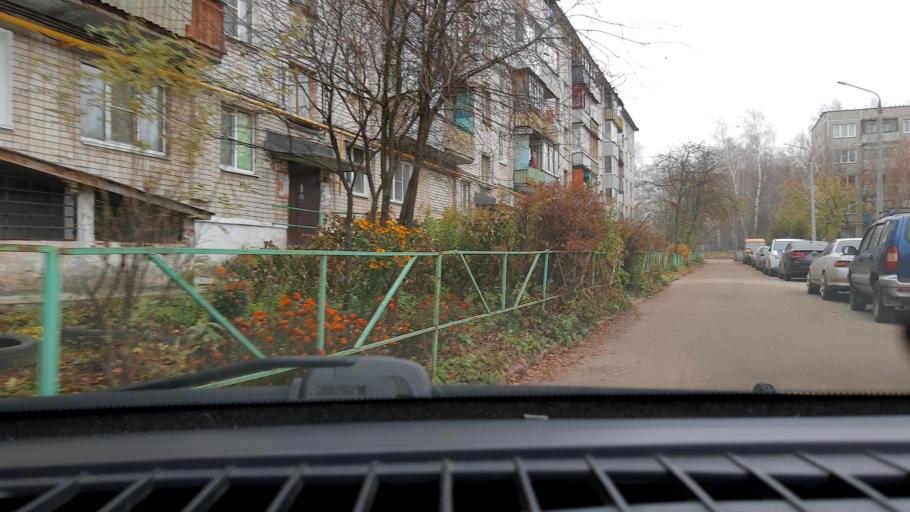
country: RU
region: Nizjnij Novgorod
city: Kstovo
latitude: 56.1816
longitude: 44.1651
